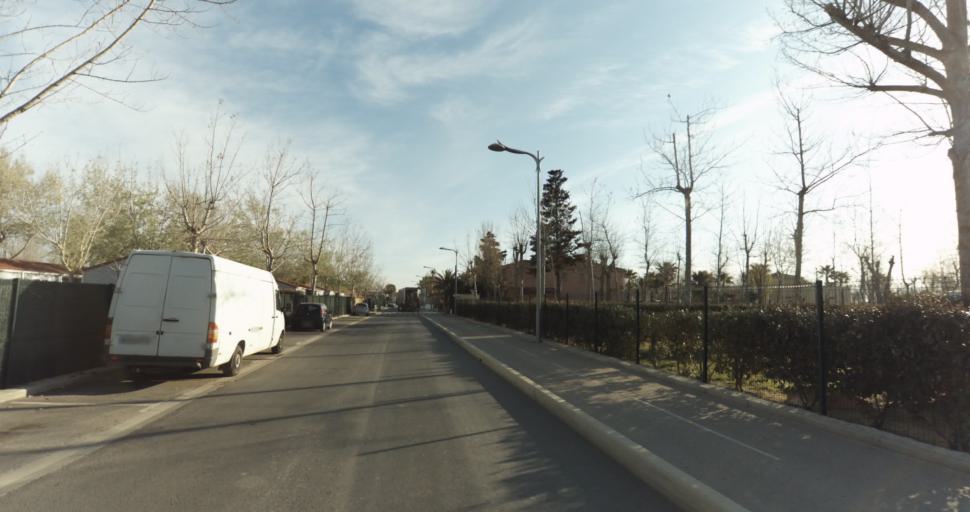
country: FR
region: Languedoc-Roussillon
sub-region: Departement de l'Herault
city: Le Cap d'Agde
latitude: 43.3088
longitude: 3.5417
